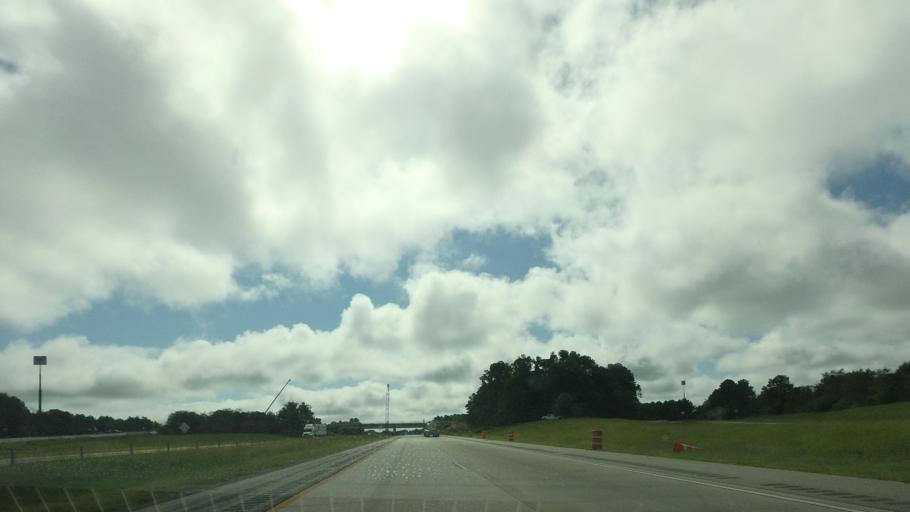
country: US
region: Georgia
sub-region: Twiggs County
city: Jeffersonville
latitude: 32.6250
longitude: -83.3727
